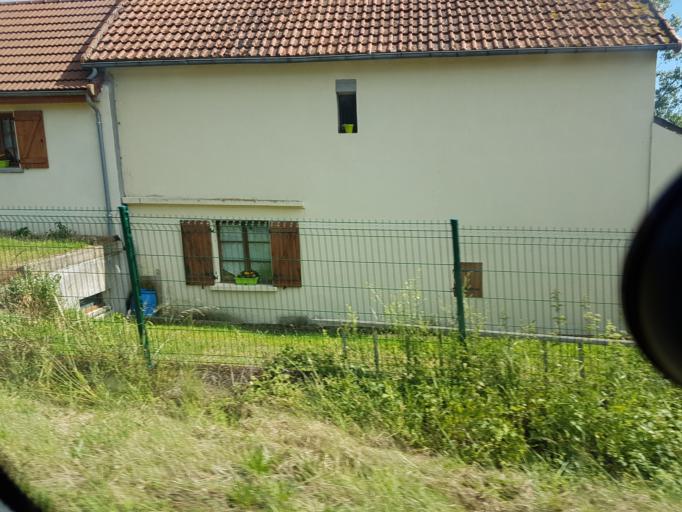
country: FR
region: Bourgogne
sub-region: Departement de Saone-et-Loire
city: Autun
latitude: 47.0516
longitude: 4.2987
